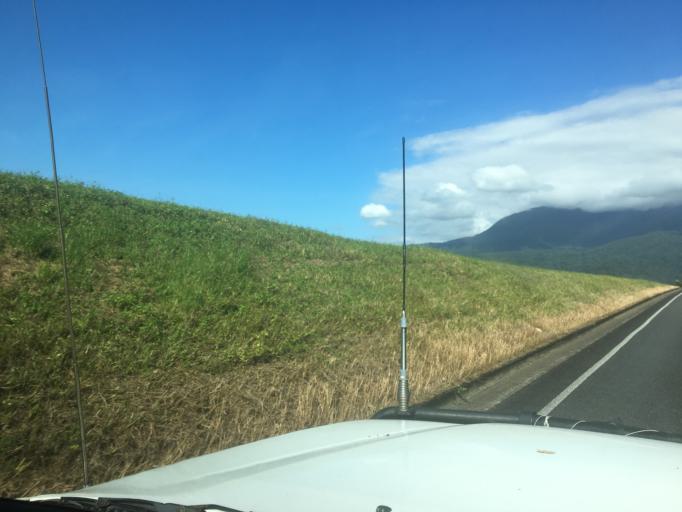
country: AU
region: Queensland
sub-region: Cassowary Coast
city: Innisfail
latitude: -17.3480
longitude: 145.9039
